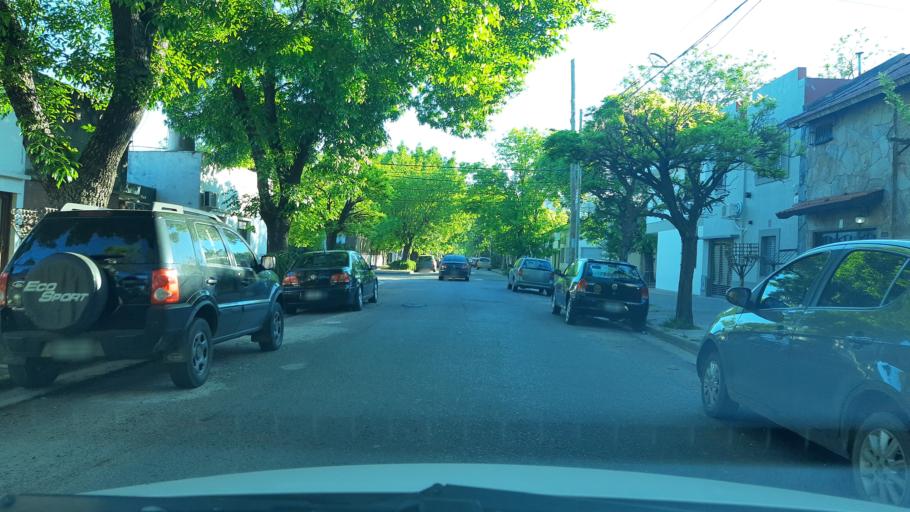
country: AR
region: Buenos Aires
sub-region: Partido de La Plata
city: La Plata
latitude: -34.9336
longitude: -57.9595
